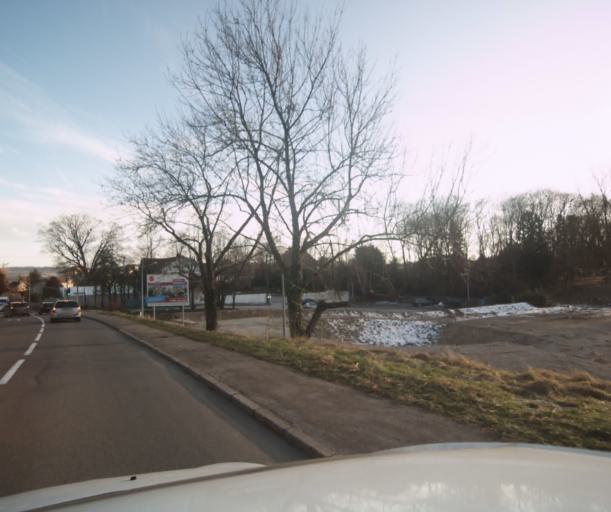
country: FR
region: Franche-Comte
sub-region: Departement du Doubs
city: Besancon
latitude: 47.2516
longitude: 6.0130
